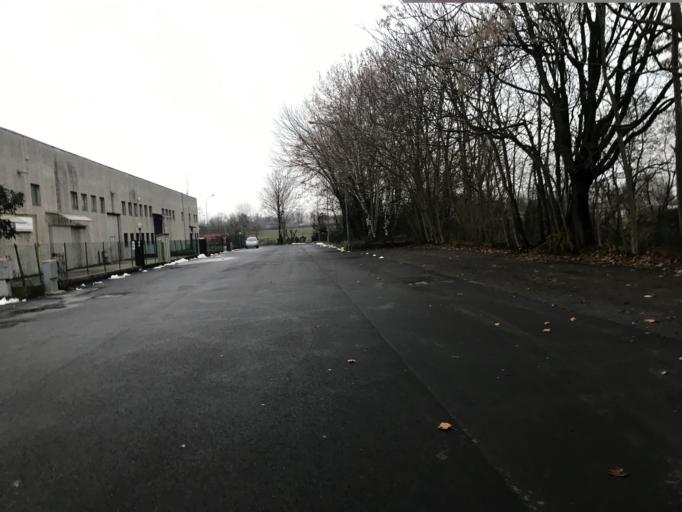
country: IT
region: Emilia-Romagna
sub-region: Provincia di Bologna
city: Progresso
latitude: 44.5390
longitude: 11.3487
